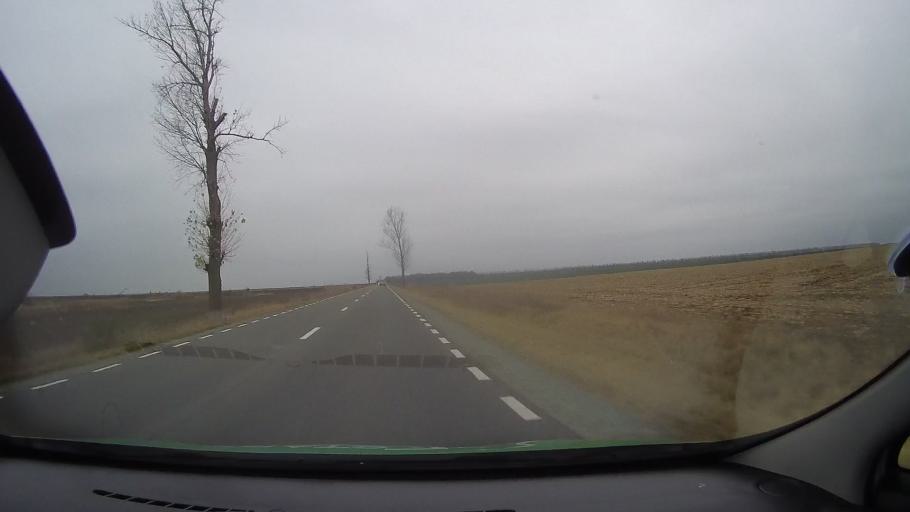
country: RO
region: Ialomita
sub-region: Comuna Scanteia
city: Iazu
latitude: 44.7110
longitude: 27.4192
